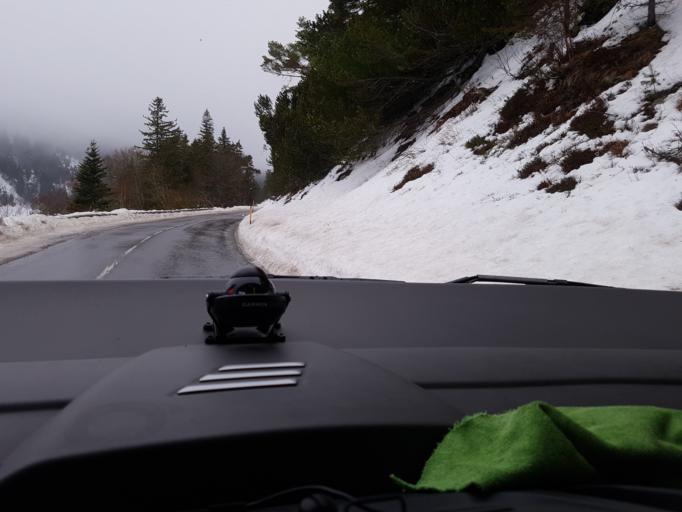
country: FR
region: Alsace
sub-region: Departement du Haut-Rhin
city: Soultzeren
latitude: 48.1257
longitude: 7.0952
